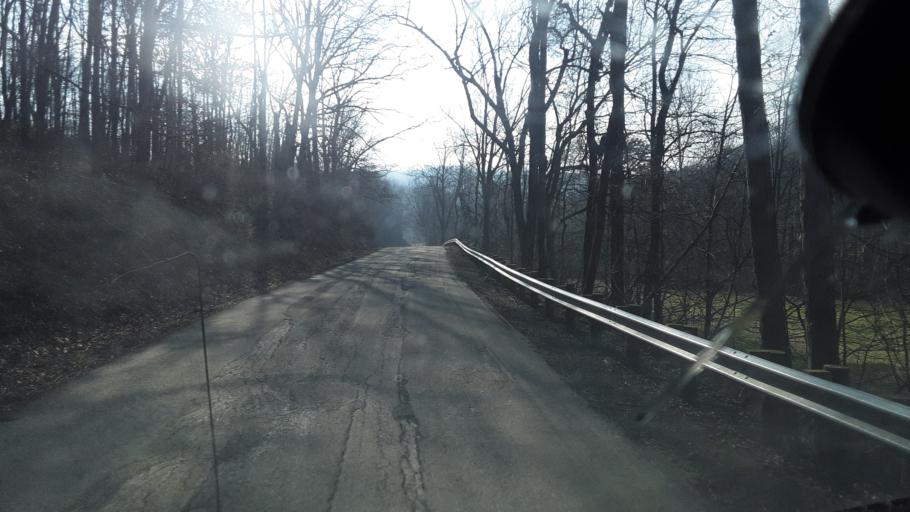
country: US
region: Ohio
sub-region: Knox County
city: Oak Hill
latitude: 40.4160
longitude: -82.2036
